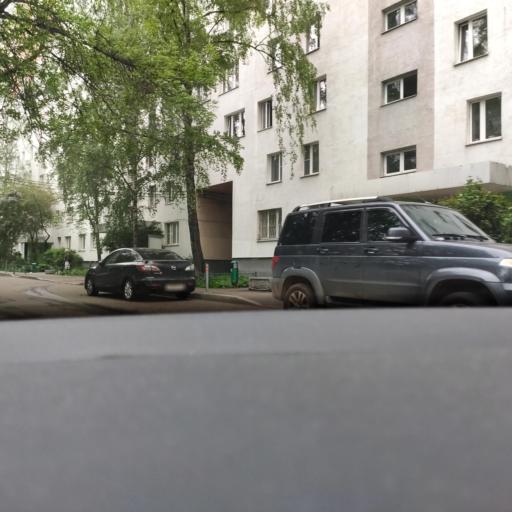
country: RU
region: Moscow
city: Vagonoremont
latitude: 55.8977
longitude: 37.5644
